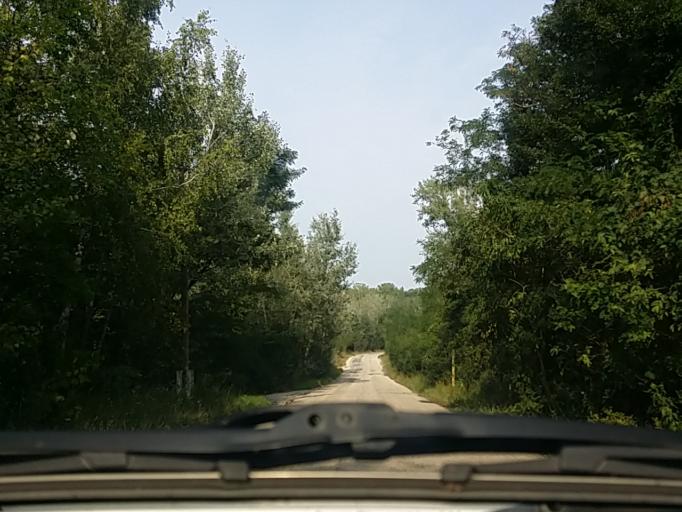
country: HU
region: Komarom-Esztergom
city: Tatabanya
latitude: 47.5278
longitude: 18.4053
